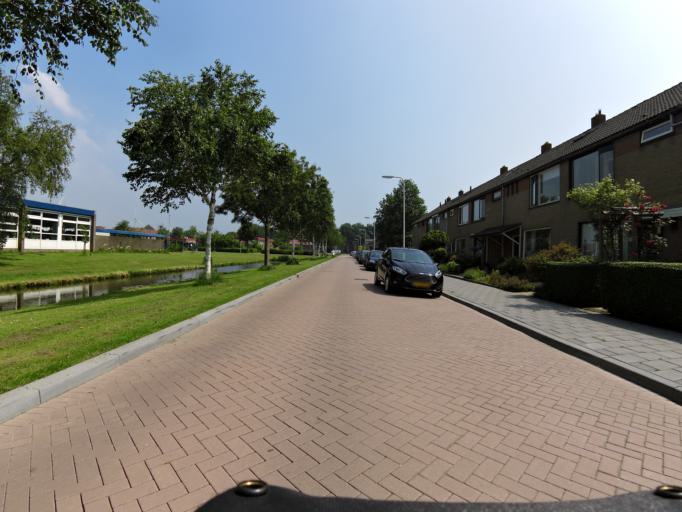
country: NL
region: South Holland
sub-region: Gemeente Maassluis
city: Maassluis
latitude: 51.8650
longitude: 4.2383
